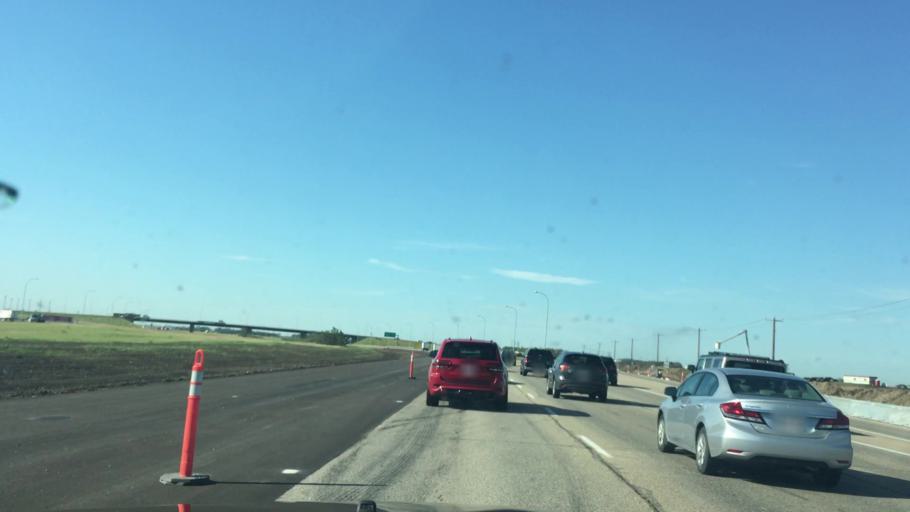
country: CA
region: Alberta
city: Leduc
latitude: 53.3447
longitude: -113.5477
